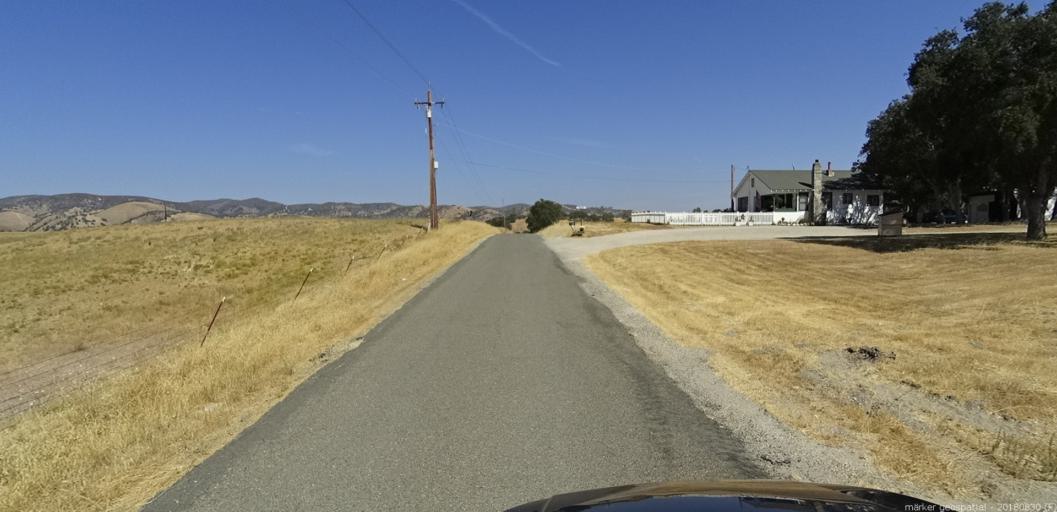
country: US
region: California
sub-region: Monterey County
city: King City
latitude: 36.0099
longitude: -121.1640
